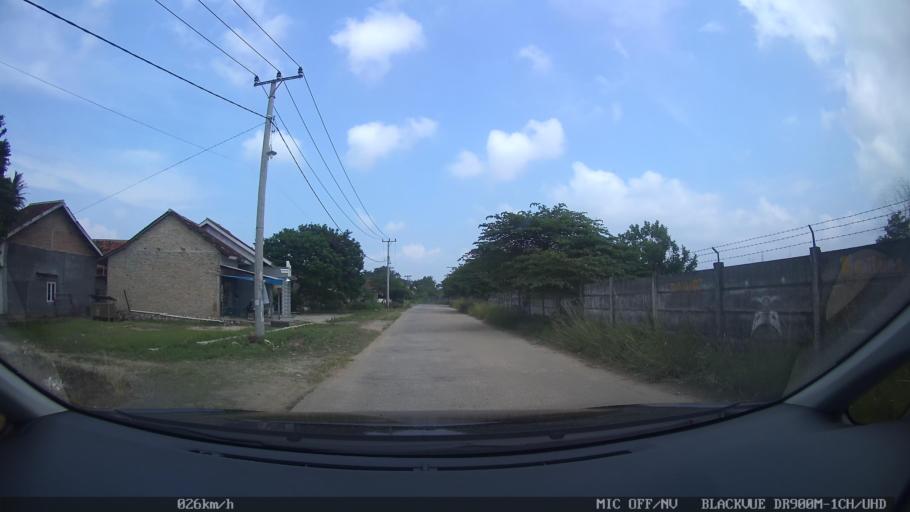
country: ID
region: Lampung
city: Kedaton
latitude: -5.3320
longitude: 105.2920
